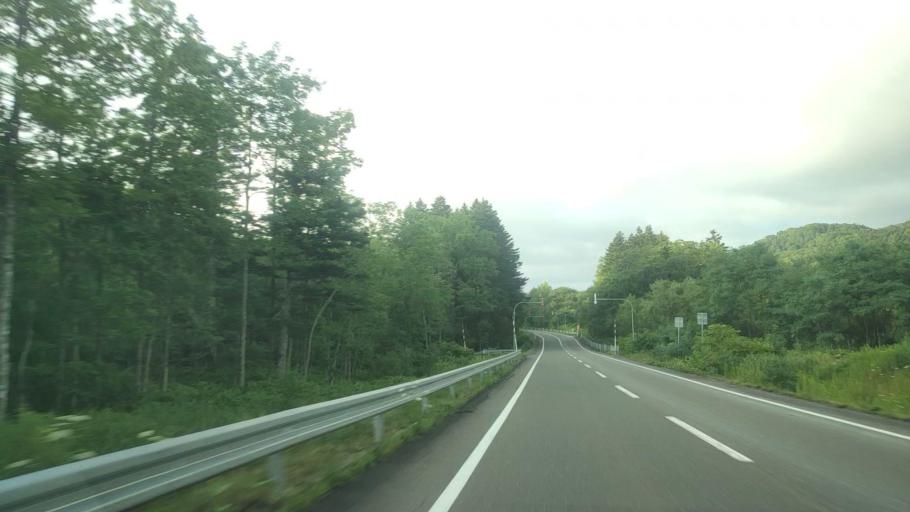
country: JP
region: Hokkaido
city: Bibai
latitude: 43.1109
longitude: 142.0991
